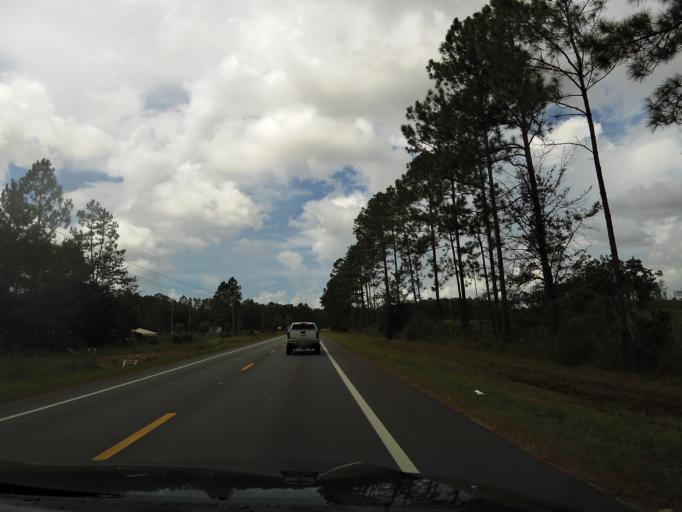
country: US
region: Florida
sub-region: Clay County
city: Middleburg
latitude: 30.0677
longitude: -81.9234
